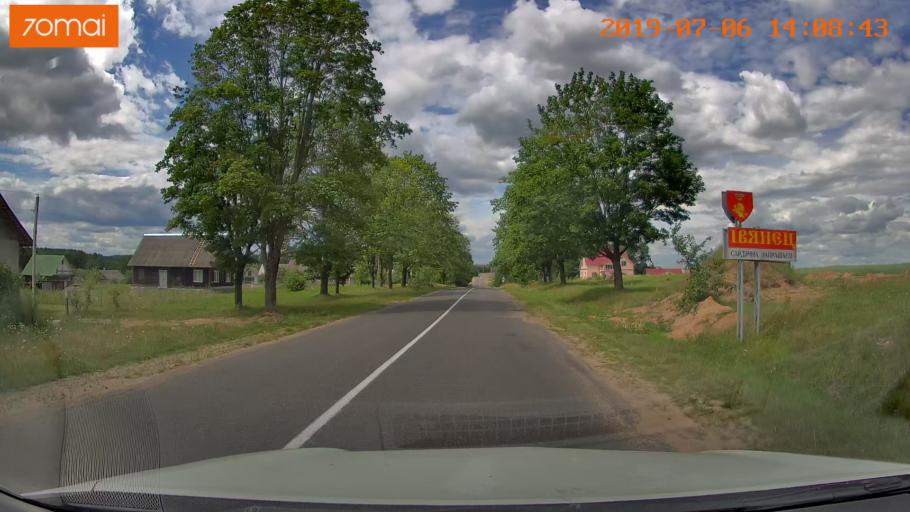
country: BY
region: Minsk
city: Ivyanyets
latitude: 53.8771
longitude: 26.7545
